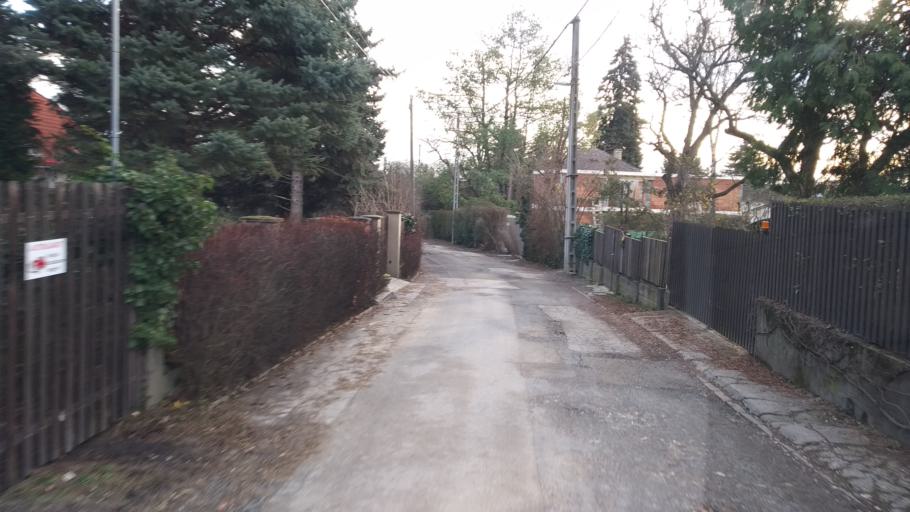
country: HU
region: Pest
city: Szentendre
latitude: 47.6882
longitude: 19.0833
